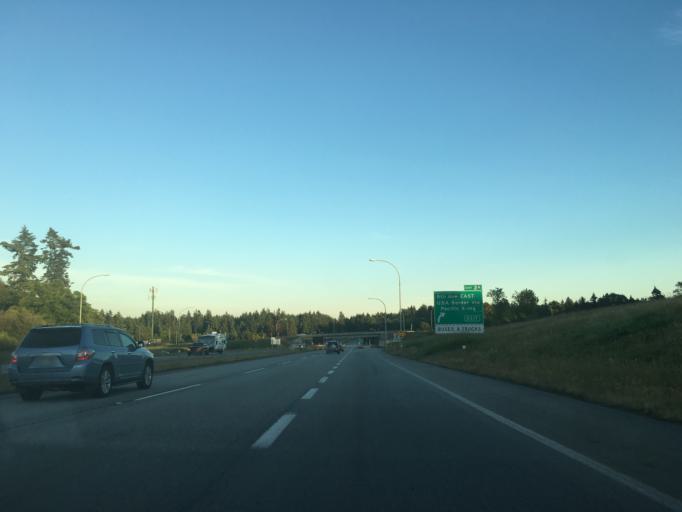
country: US
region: Washington
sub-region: Whatcom County
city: Blaine
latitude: 49.0197
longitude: -122.7615
